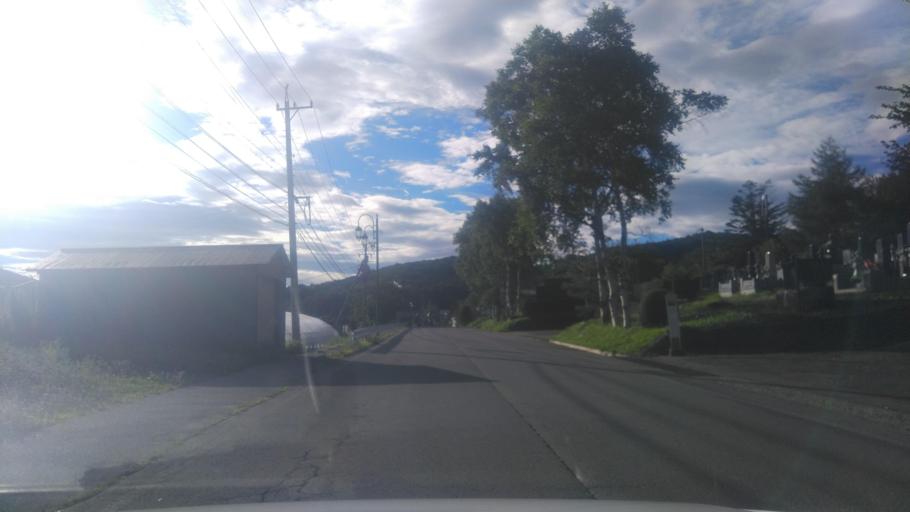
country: JP
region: Nagano
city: Suzaka
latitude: 36.5319
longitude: 138.3292
